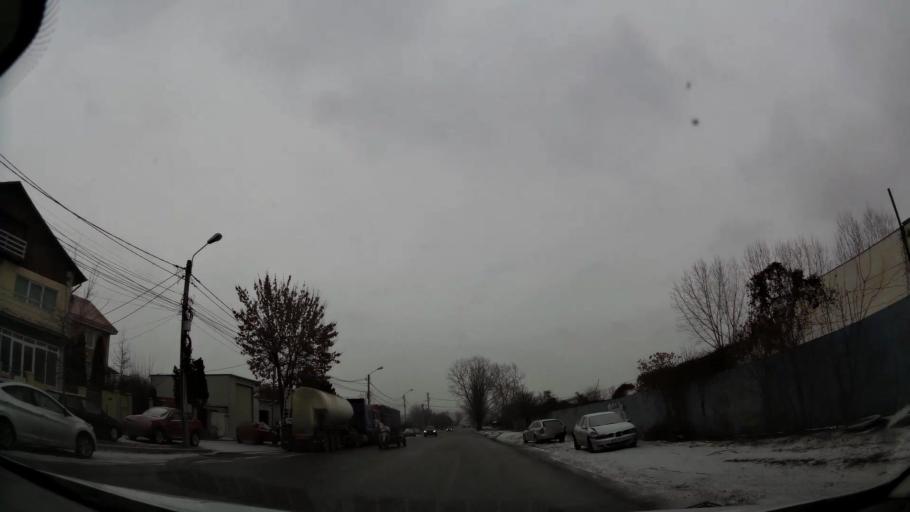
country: RO
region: Dambovita
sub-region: Municipiul Targoviste
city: Targoviste
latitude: 44.9195
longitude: 25.4815
